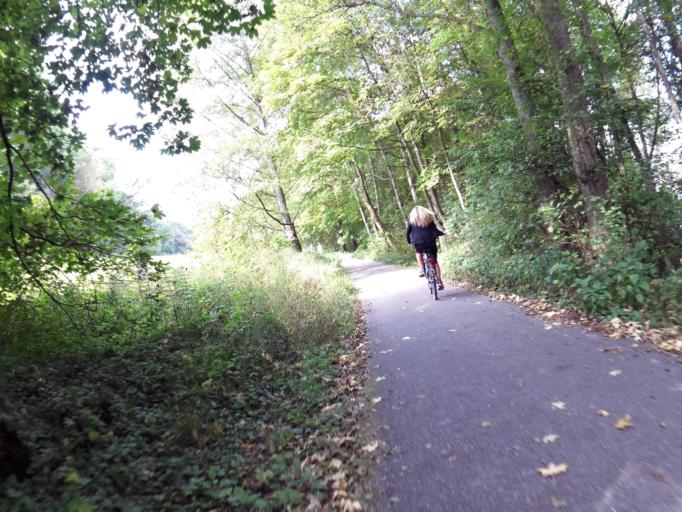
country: DE
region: Bavaria
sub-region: Upper Bavaria
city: Bernried
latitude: 47.8633
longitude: 11.2998
